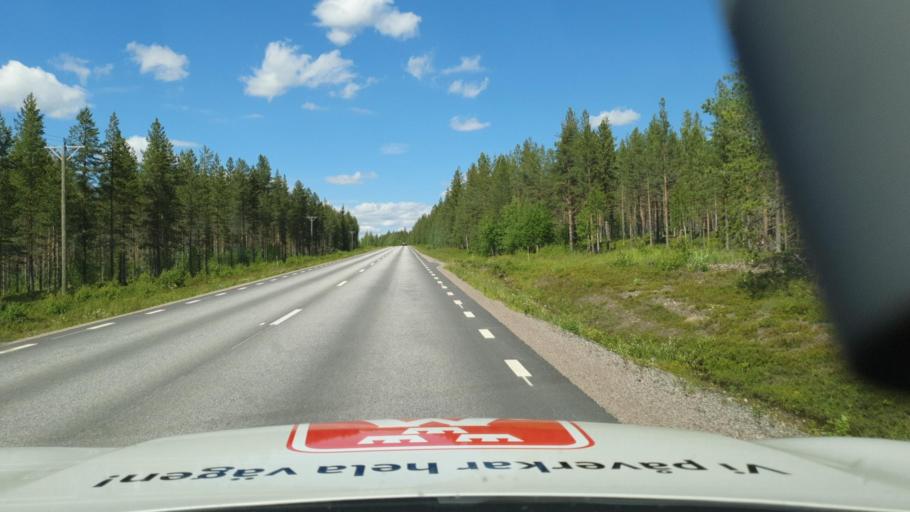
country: SE
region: Vaesterbotten
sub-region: Skelleftea Kommun
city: Langsele
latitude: 64.9509
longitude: 20.2671
